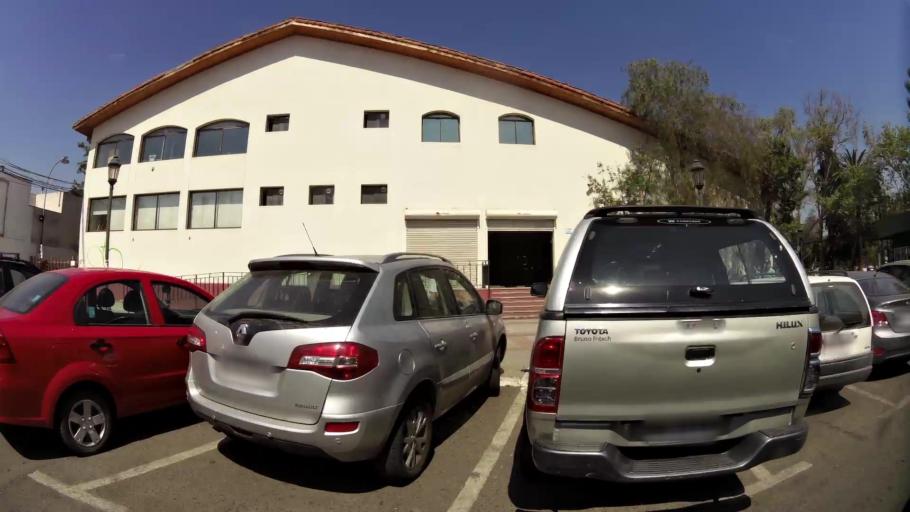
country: CL
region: Santiago Metropolitan
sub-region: Provincia de Maipo
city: San Bernardo
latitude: -33.5920
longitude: -70.7034
